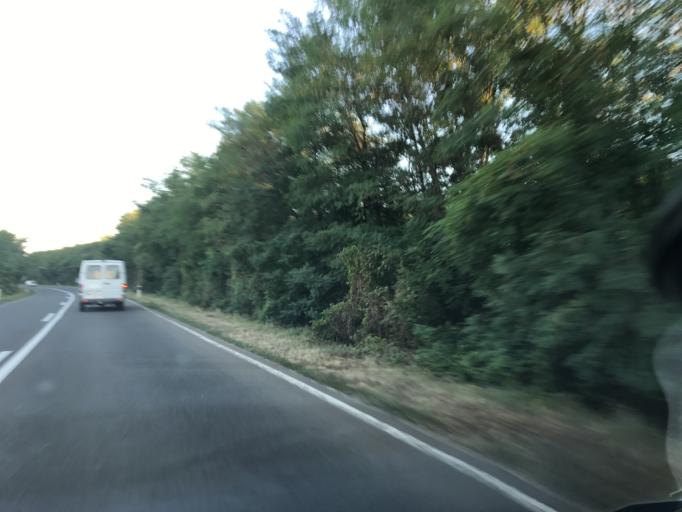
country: RS
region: Central Serbia
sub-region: Branicevski Okrug
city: Pozarevac
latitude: 44.6494
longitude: 21.2068
